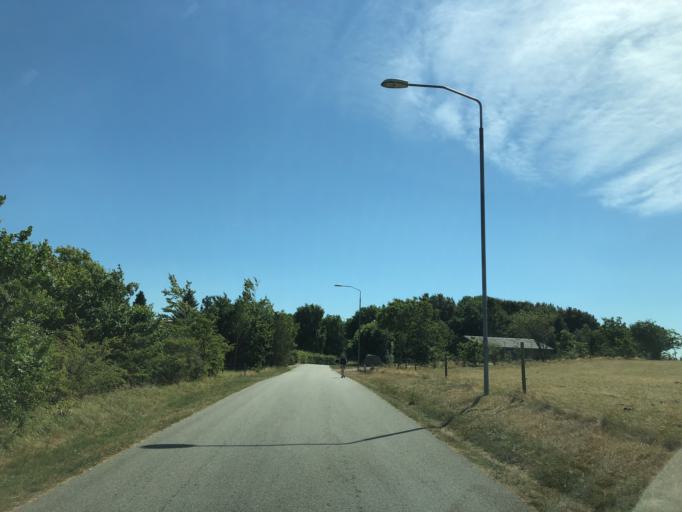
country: DK
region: Central Jutland
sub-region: Skive Kommune
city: Skive
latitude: 56.5452
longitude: 9.0118
